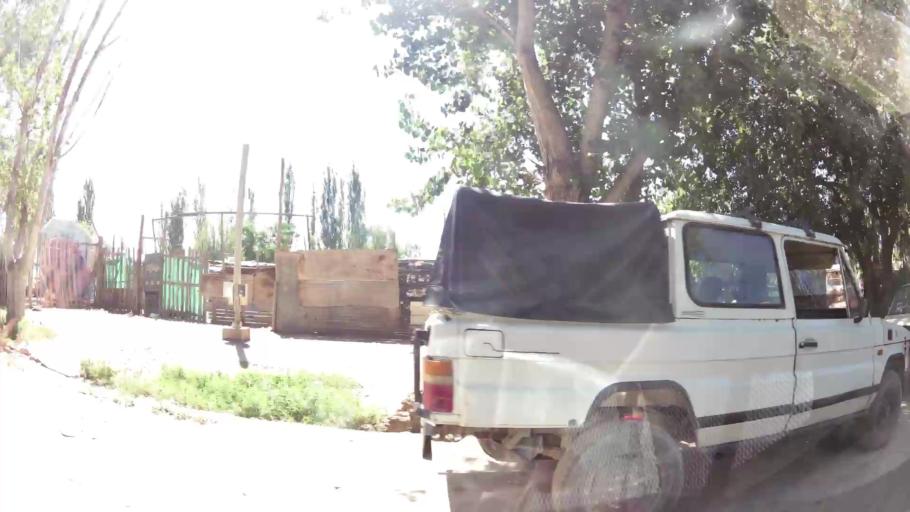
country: AR
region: Mendoza
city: Villa Nueva
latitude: -32.8745
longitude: -68.7869
